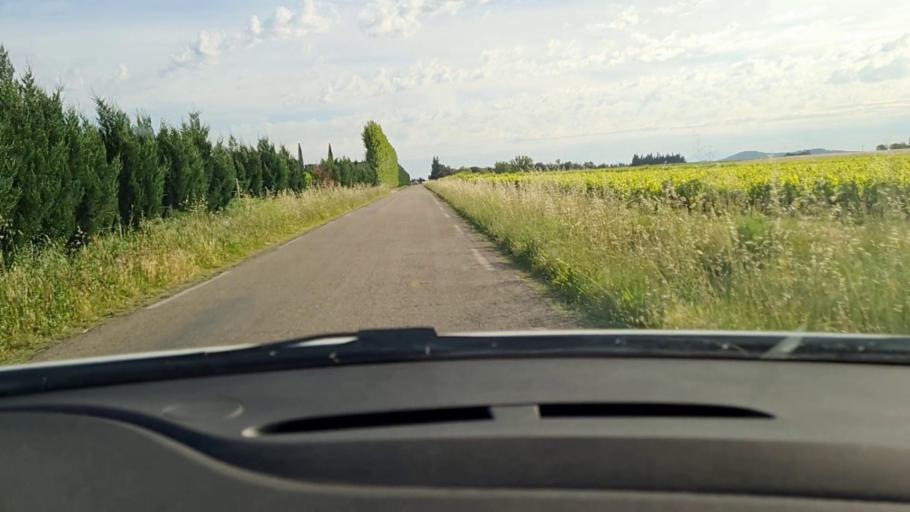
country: FR
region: Languedoc-Roussillon
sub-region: Departement du Gard
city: Jonquieres-Saint-Vincent
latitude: 43.8092
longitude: 4.5447
